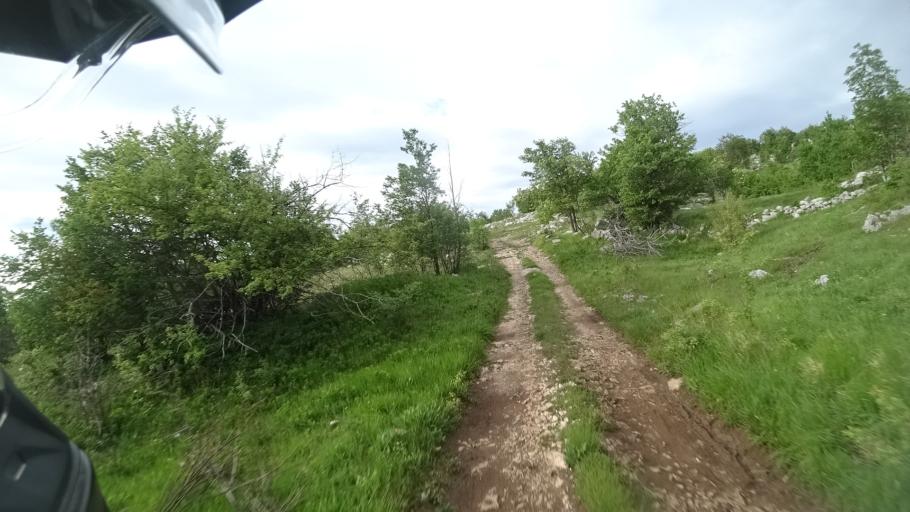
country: HR
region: Sibensko-Kniniska
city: Drnis
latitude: 43.8663
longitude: 16.3925
